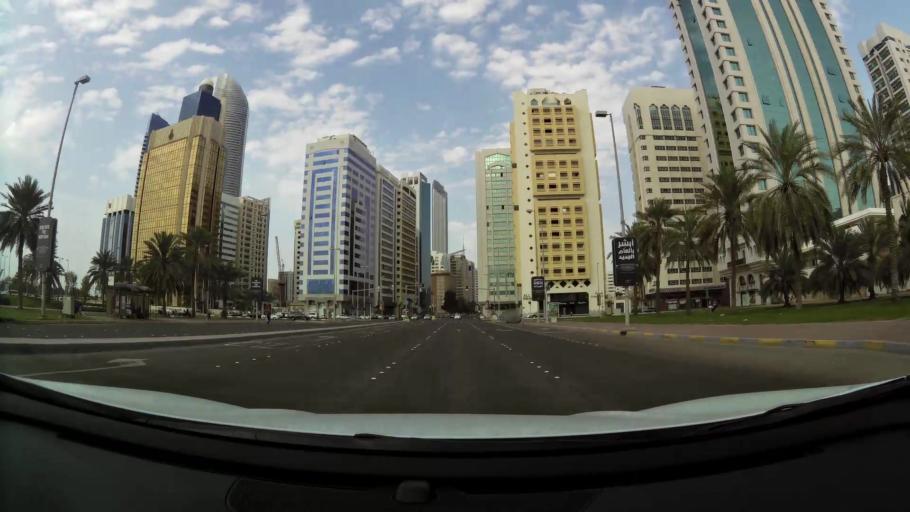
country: AE
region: Abu Dhabi
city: Abu Dhabi
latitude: 24.4797
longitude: 54.3500
